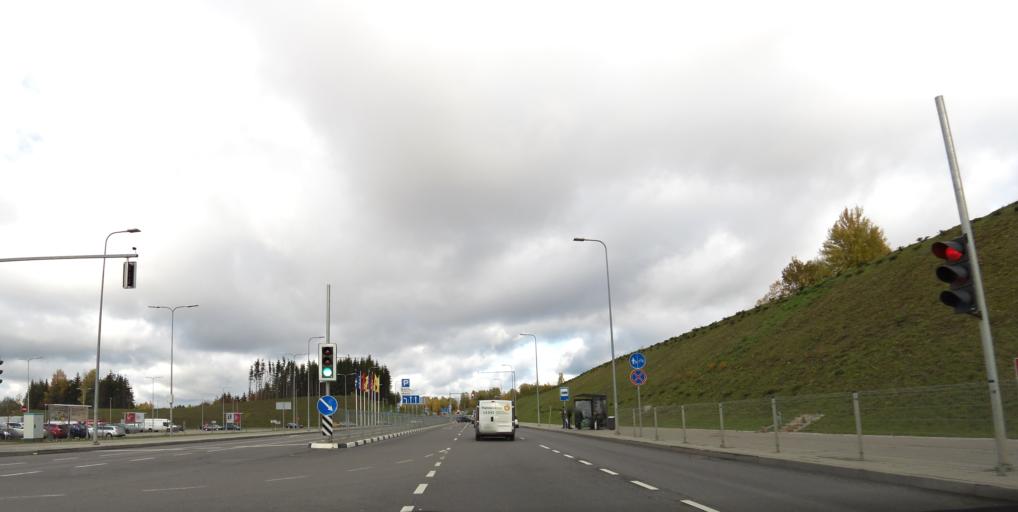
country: LT
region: Vilnius County
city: Naujamiestis
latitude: 54.6514
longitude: 25.2823
